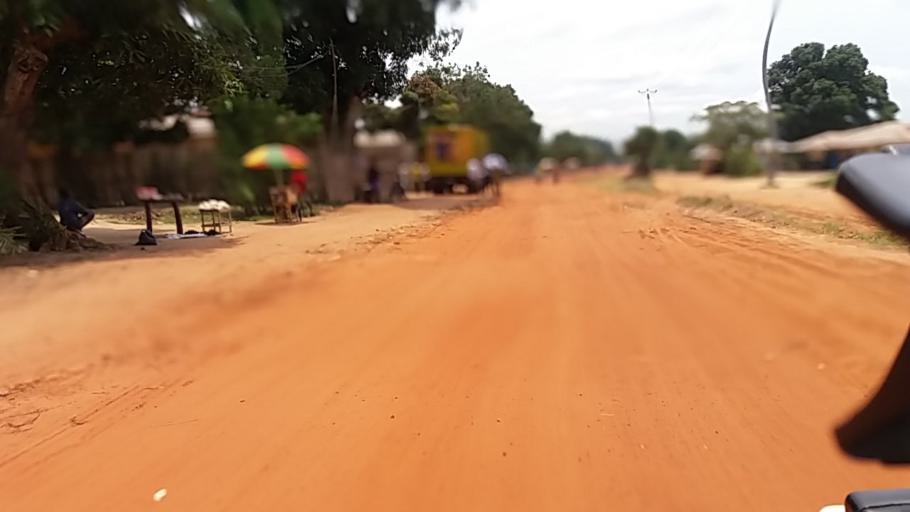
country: CD
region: Bandundu
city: Bandundu
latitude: -3.3209
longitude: 17.3956
